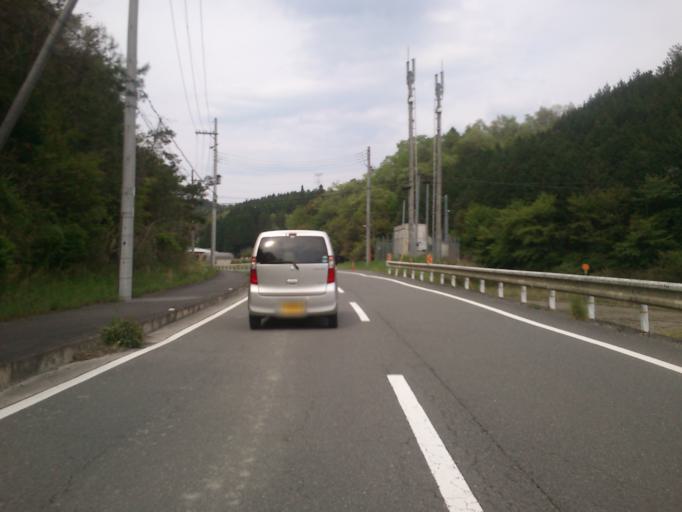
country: JP
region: Kyoto
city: Kameoka
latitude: 34.9528
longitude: 135.5519
